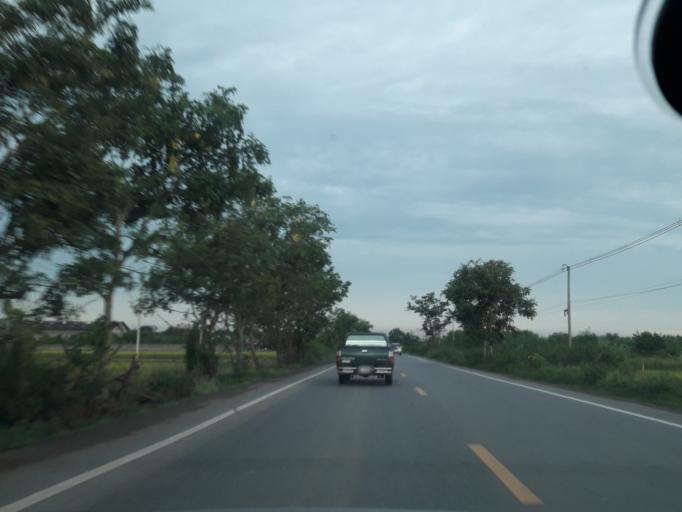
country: TH
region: Phra Nakhon Si Ayutthaya
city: Wang Noi
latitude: 14.1697
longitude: 100.7474
